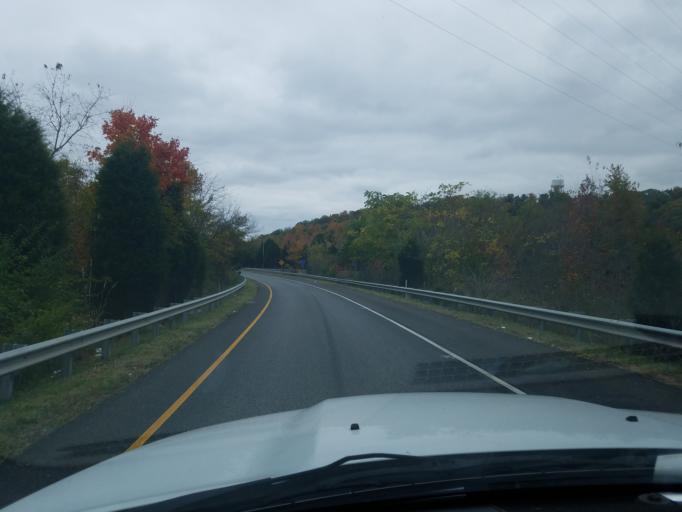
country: US
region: Indiana
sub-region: Floyd County
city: New Albany
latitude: 38.3011
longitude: -85.8497
